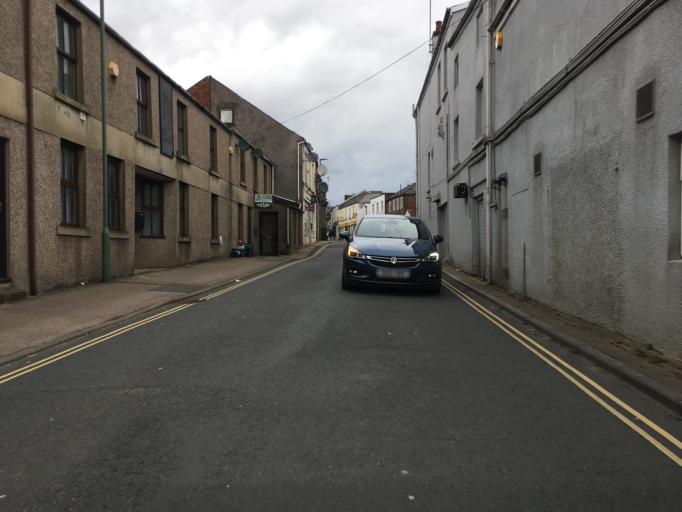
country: GB
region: England
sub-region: Gloucestershire
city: Cinderford
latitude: 51.8230
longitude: -2.5003
